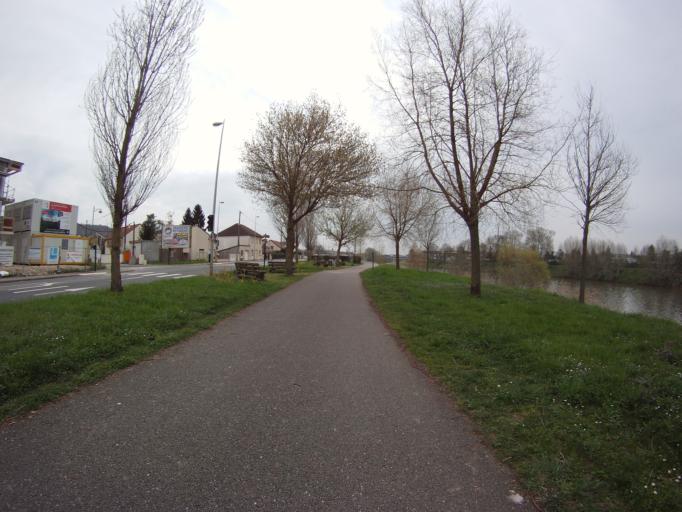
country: FR
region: Lorraine
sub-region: Departement de Meurthe-et-Moselle
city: Malzeville
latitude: 48.7138
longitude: 6.1755
